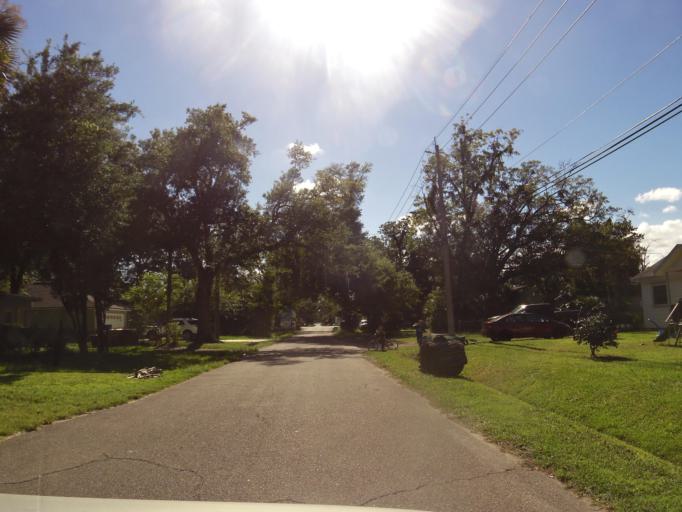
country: US
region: Florida
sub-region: Duval County
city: Jacksonville
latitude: 30.2813
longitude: -81.7246
